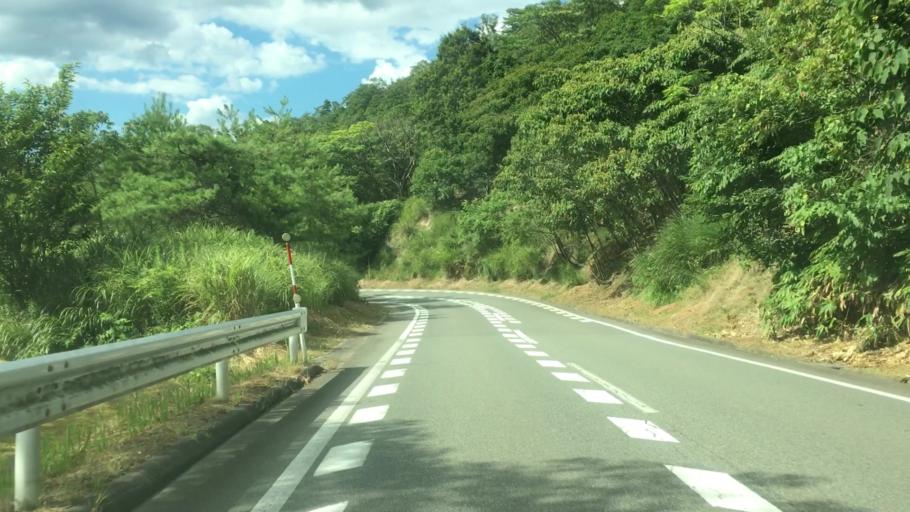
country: JP
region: Hyogo
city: Toyooka
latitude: 35.5231
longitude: 134.7916
